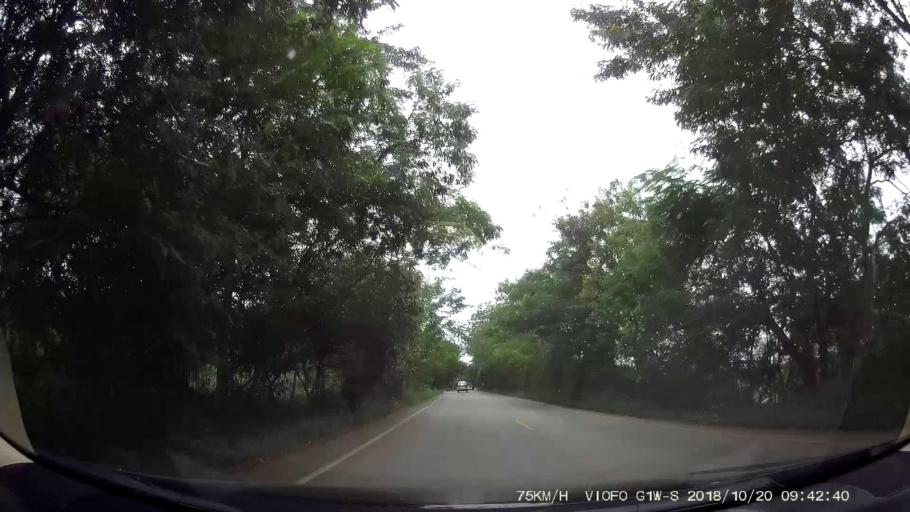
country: TH
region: Chaiyaphum
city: Khon San
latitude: 16.4662
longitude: 101.9513
